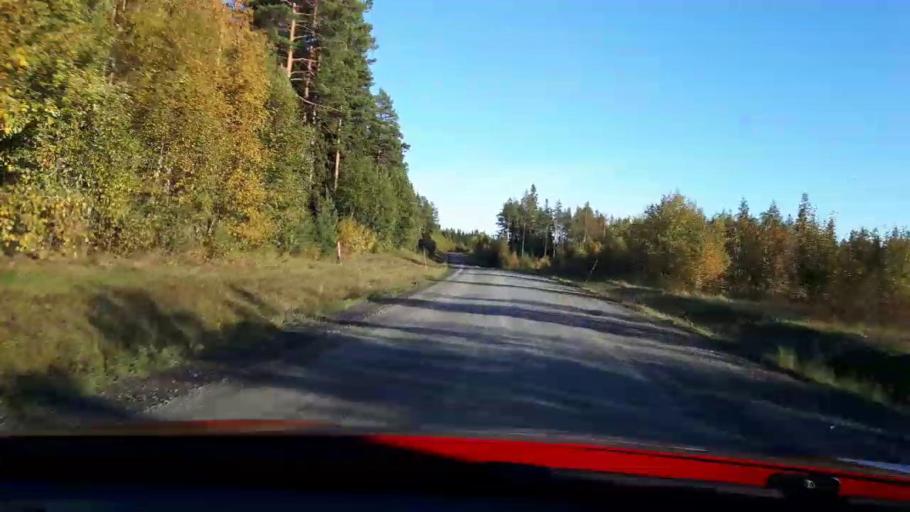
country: SE
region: Jaemtland
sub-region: OEstersunds Kommun
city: Lit
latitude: 63.6706
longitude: 14.6966
